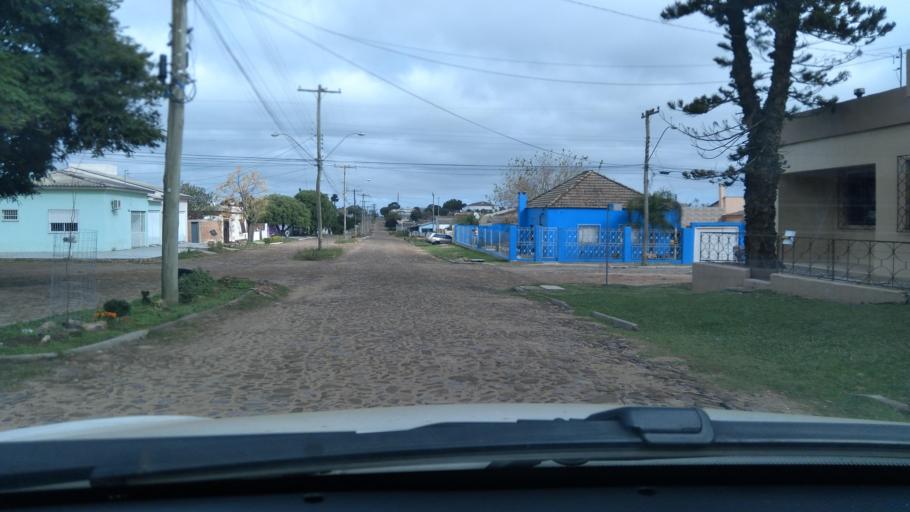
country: BR
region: Rio Grande do Sul
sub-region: Dom Pedrito
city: Dom Pedrito
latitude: -30.9820
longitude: -54.6624
